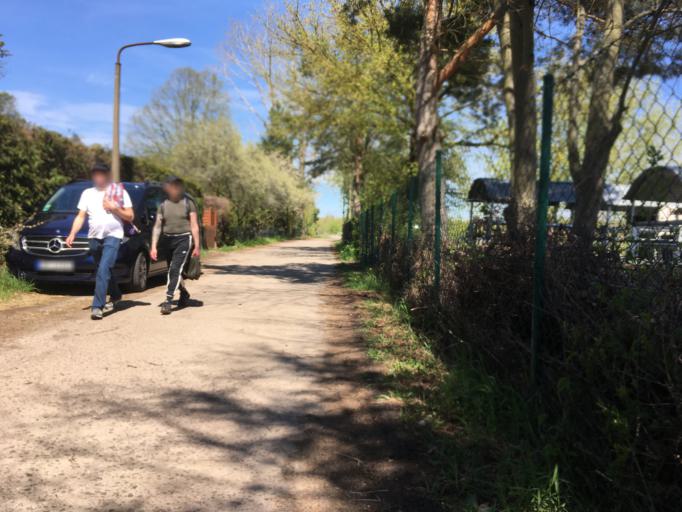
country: DE
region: Berlin
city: Buch
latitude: 52.6656
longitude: 13.4901
